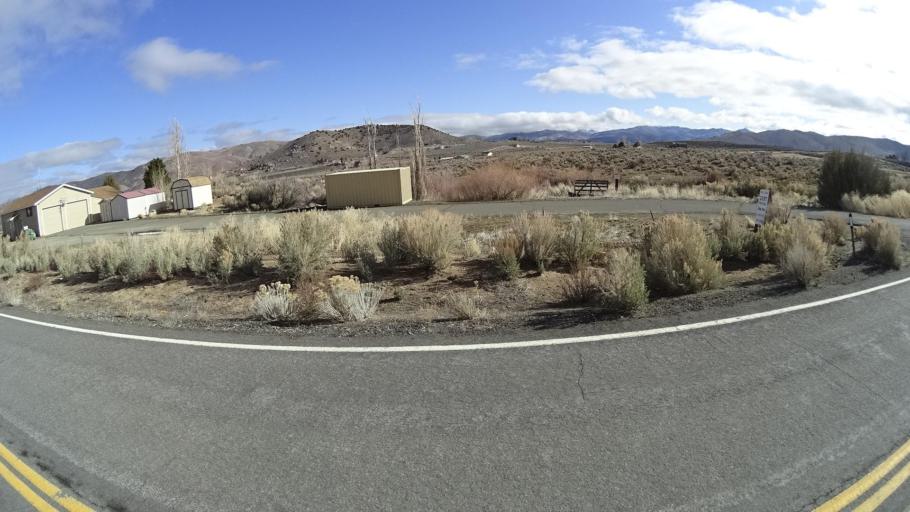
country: US
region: Nevada
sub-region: Washoe County
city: Cold Springs
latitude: 39.8692
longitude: -119.9604
